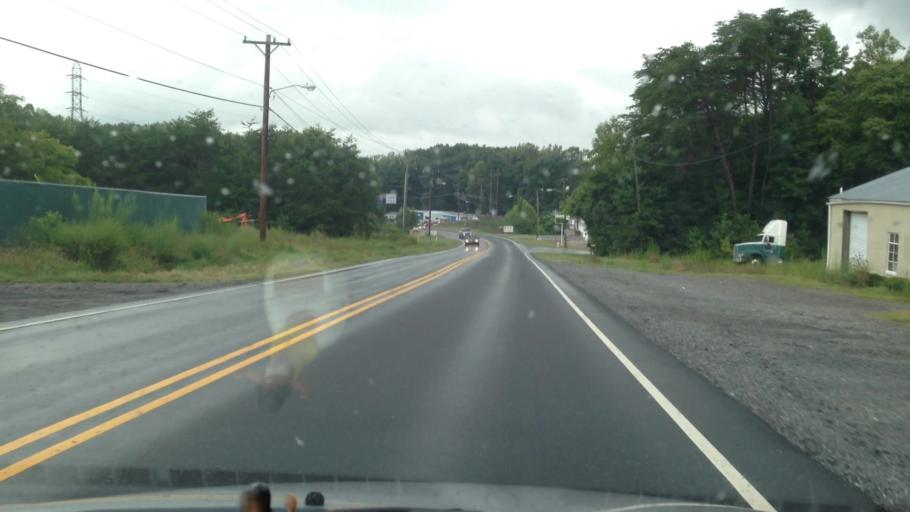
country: US
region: North Carolina
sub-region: Rockingham County
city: Madison
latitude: 36.3826
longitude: -79.9490
